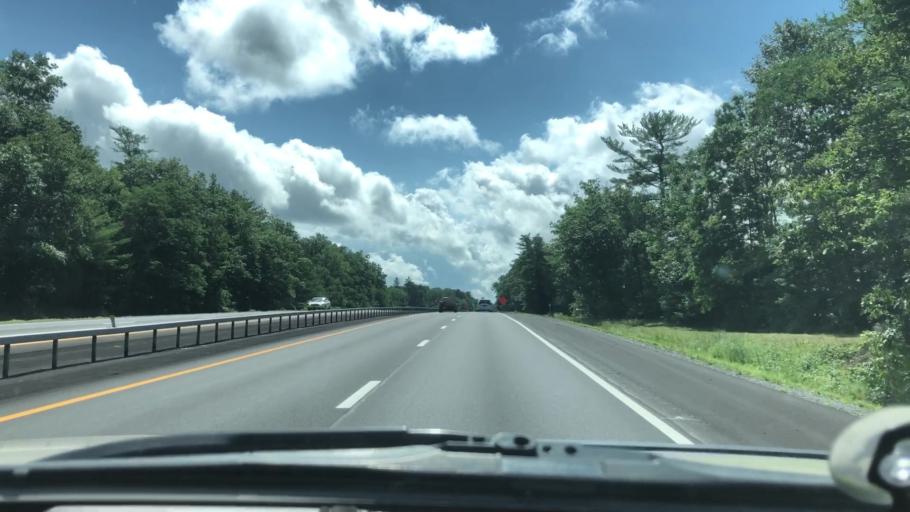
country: US
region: New York
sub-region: Greene County
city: Cairo
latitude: 42.3045
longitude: -73.9989
